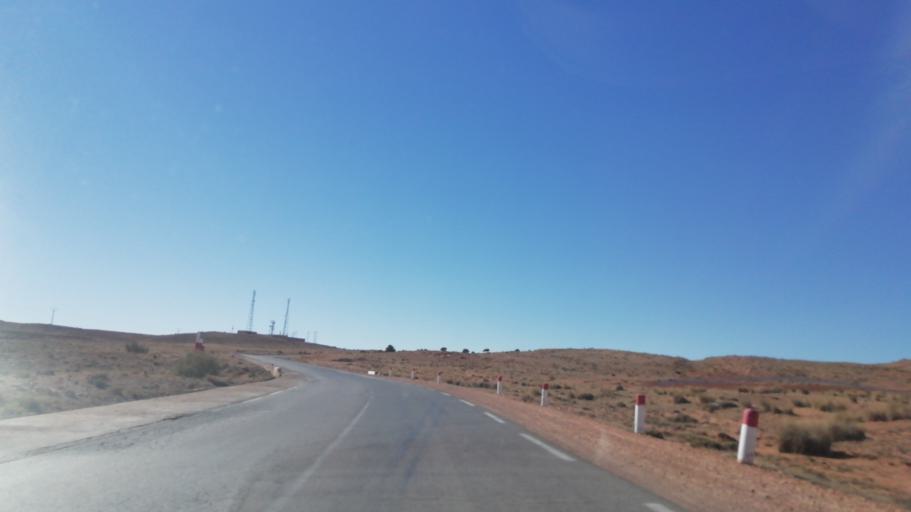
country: DZ
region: El Bayadh
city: El Bayadh
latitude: 33.6647
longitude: 1.4294
